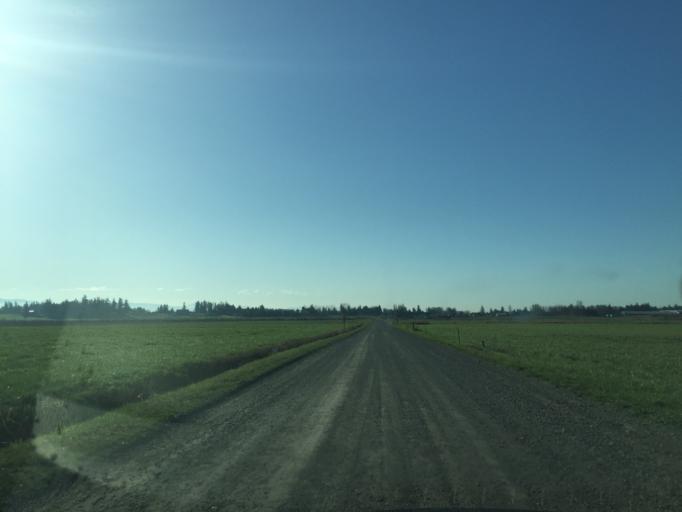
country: US
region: Washington
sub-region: Whatcom County
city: Lynden
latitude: 48.9242
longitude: -122.4640
